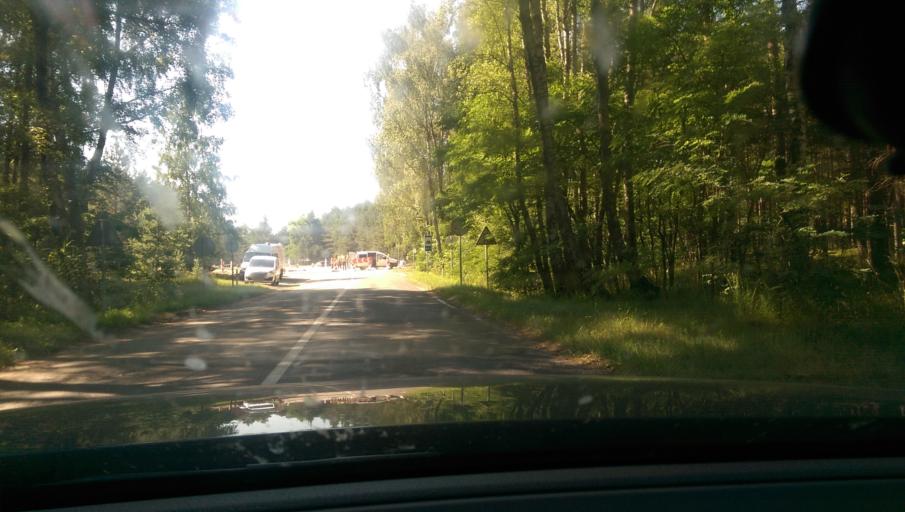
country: LT
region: Klaipedos apskritis
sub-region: Klaipeda
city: Klaipeda
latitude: 55.6798
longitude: 21.1134
